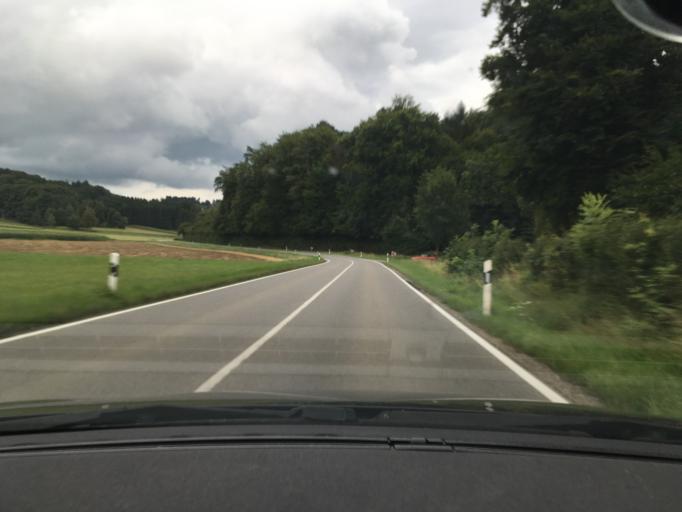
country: DE
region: Baden-Wuerttemberg
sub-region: Tuebingen Region
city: Markdorf
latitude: 47.7723
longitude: 9.4098
